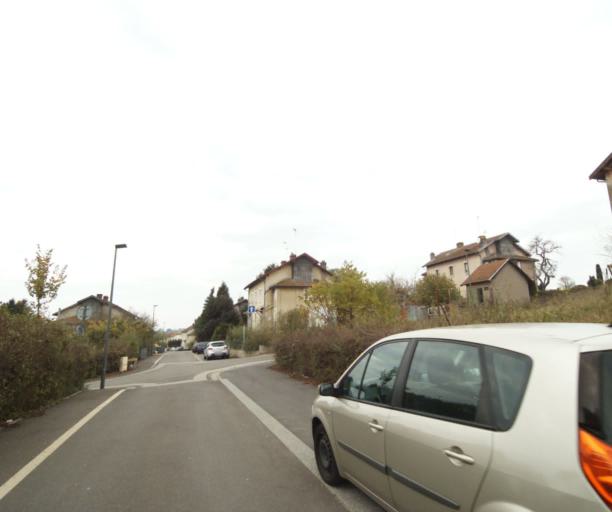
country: FR
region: Lorraine
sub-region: Departement de Meurthe-et-Moselle
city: Mancieulles
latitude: 49.2880
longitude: 5.9005
